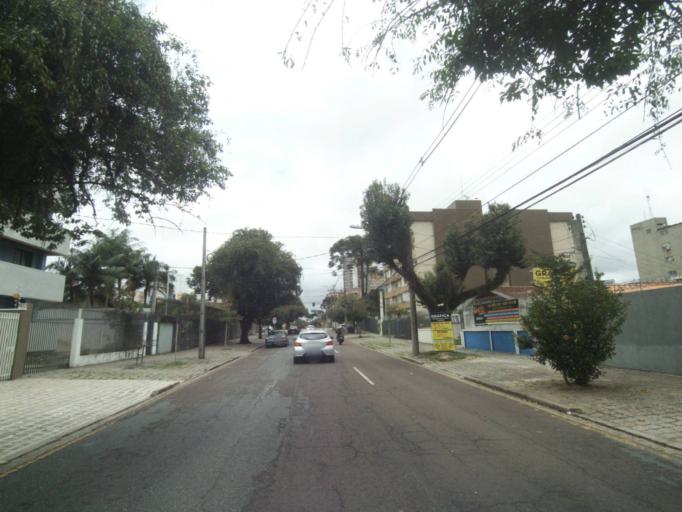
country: BR
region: Parana
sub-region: Curitiba
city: Curitiba
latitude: -25.4298
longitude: -49.2555
